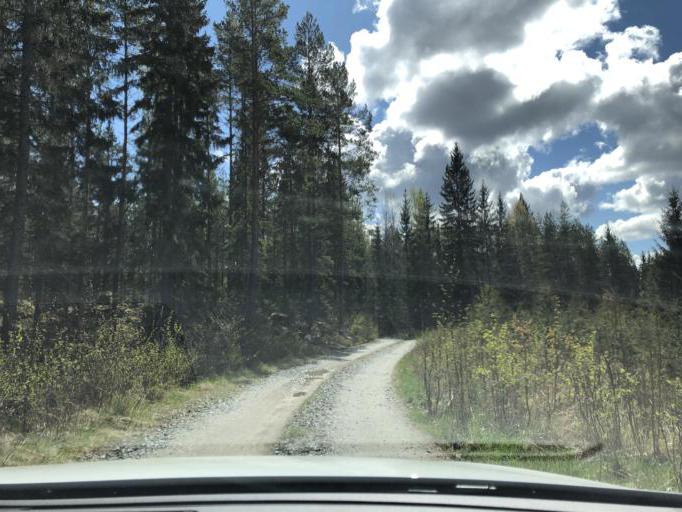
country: SE
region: Uppsala
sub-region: Heby Kommun
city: Tarnsjo
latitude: 60.2385
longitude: 16.7060
